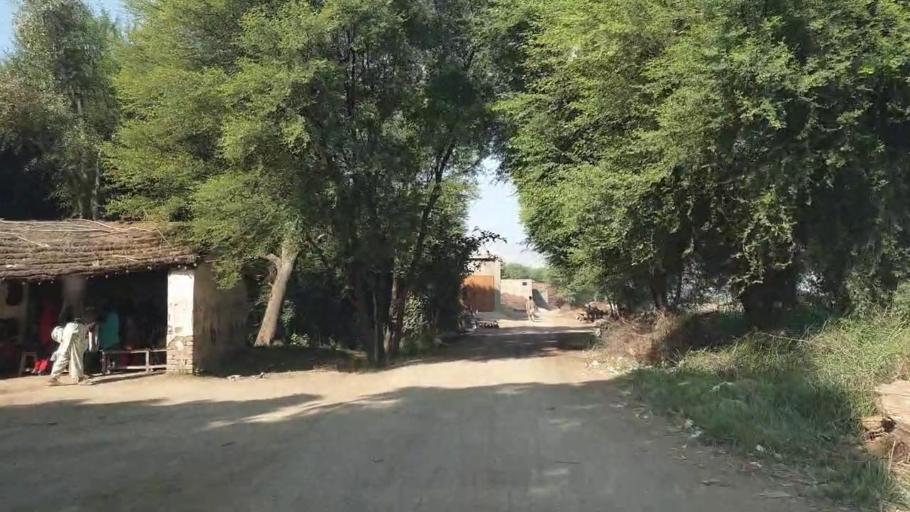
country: PK
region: Sindh
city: Matiari
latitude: 25.6795
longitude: 68.3471
